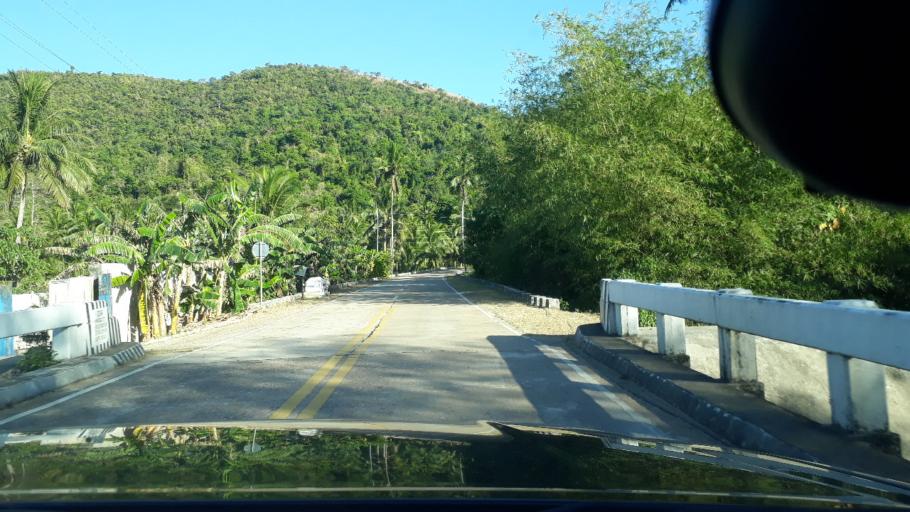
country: PH
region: Mimaropa
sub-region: Province of Palawan
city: Coron
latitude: 12.0475
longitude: 120.1555
